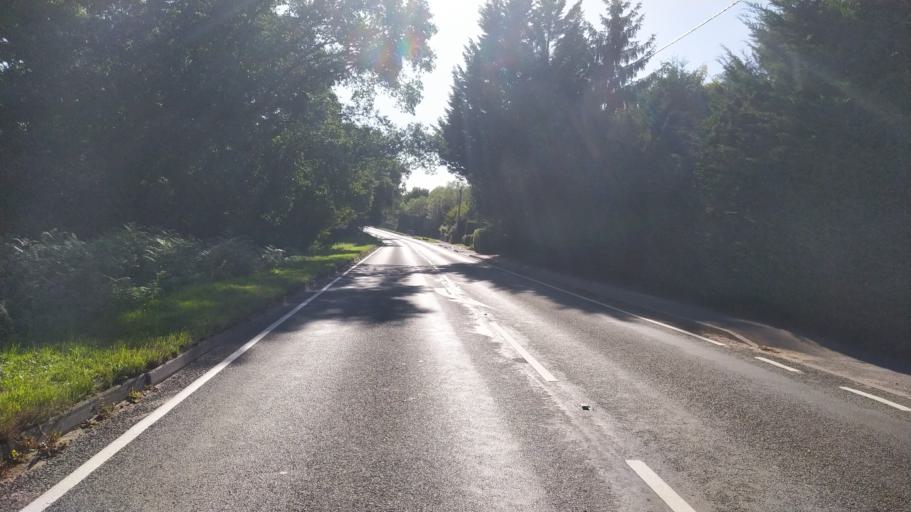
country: GB
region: England
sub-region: Hampshire
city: Kingsley
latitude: 51.1370
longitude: -0.8769
